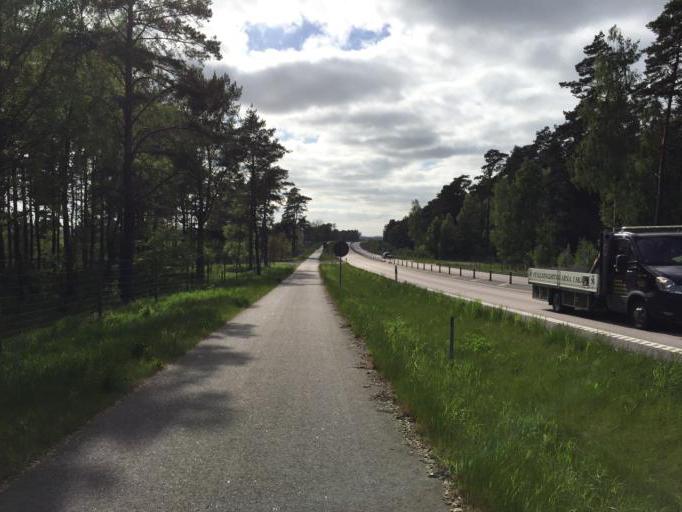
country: SE
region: Skane
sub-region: Sjobo Kommun
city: Blentarp
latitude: 55.6381
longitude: 13.5781
